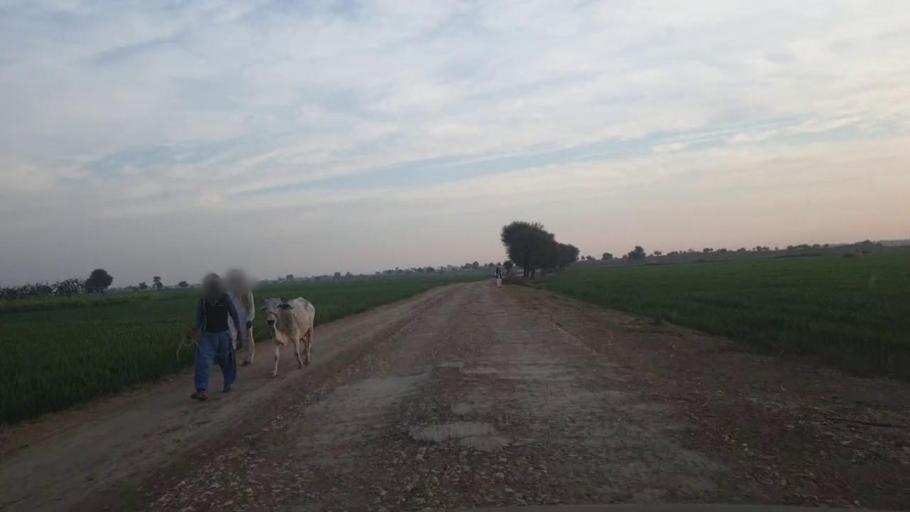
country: PK
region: Sindh
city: Shahpur Chakar
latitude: 26.0639
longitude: 68.5282
